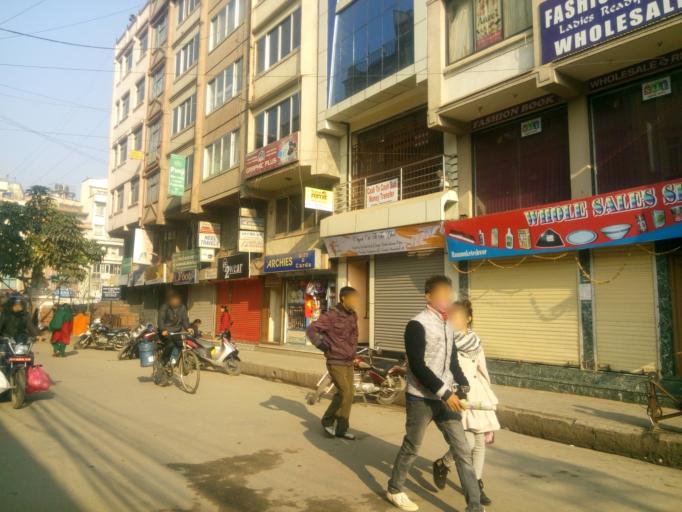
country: NP
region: Central Region
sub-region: Bagmati Zone
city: Kathmandu
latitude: 27.7015
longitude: 85.3094
